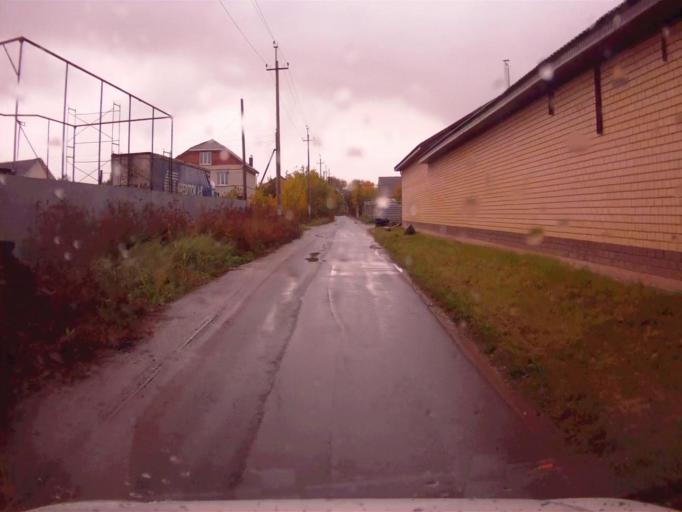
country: RU
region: Chelyabinsk
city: Dolgoderevenskoye
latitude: 55.3050
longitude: 61.3404
